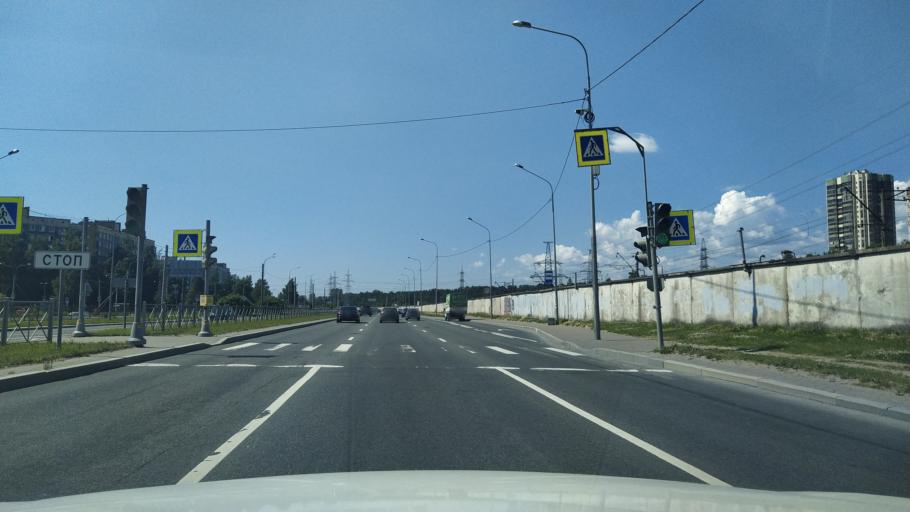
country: RU
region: St.-Petersburg
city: Ozerki
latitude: 60.0662
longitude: 30.3150
